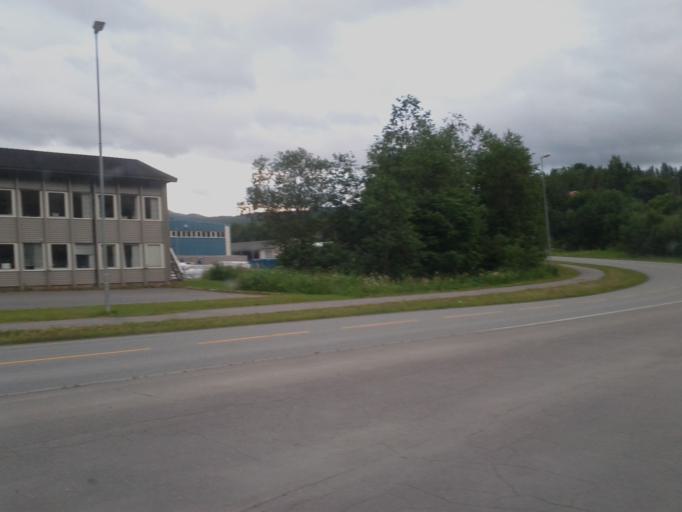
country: NO
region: Sor-Trondelag
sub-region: Midtre Gauldal
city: Storen
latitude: 63.0449
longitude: 10.2825
